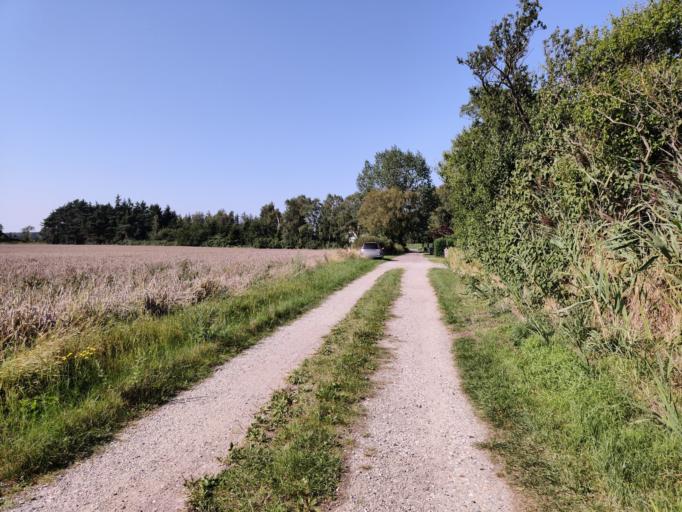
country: DK
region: Zealand
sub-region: Guldborgsund Kommune
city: Nykobing Falster
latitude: 54.6805
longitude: 11.9087
